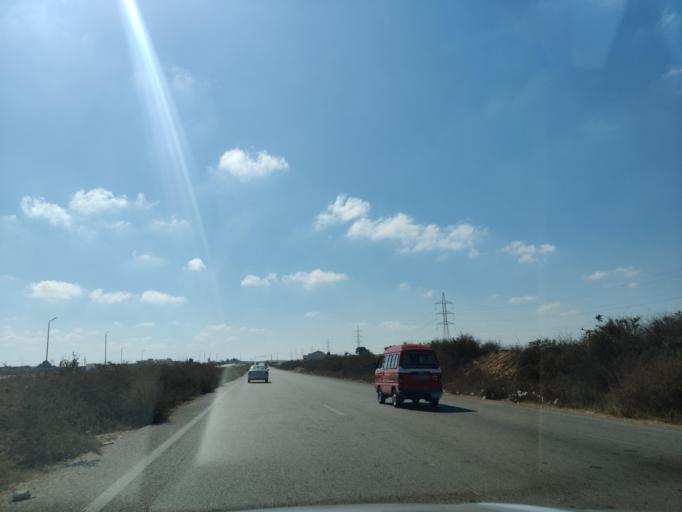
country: EG
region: Muhafazat Matruh
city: Al `Alamayn
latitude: 31.0460
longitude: 28.3419
